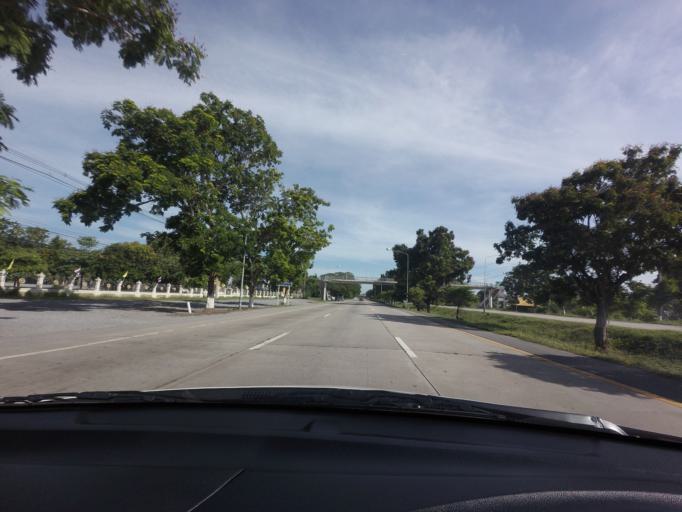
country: TH
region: Suphan Buri
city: Bang Pla Ma
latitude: 14.3973
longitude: 100.1668
